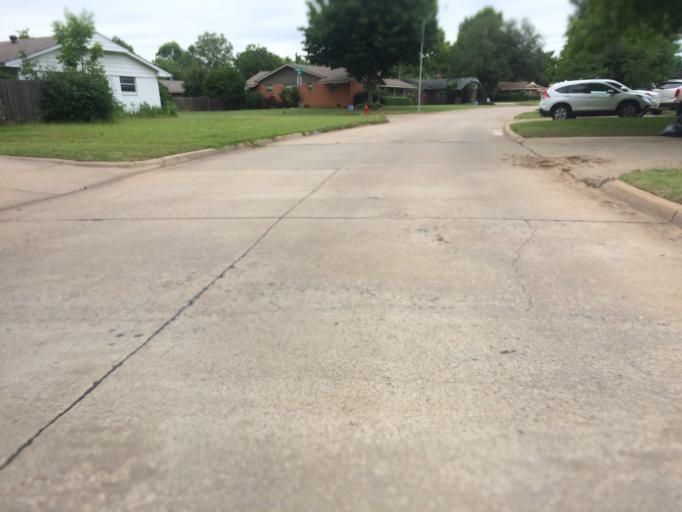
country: US
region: Oklahoma
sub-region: Cleveland County
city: Norman
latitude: 35.2120
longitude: -97.4786
